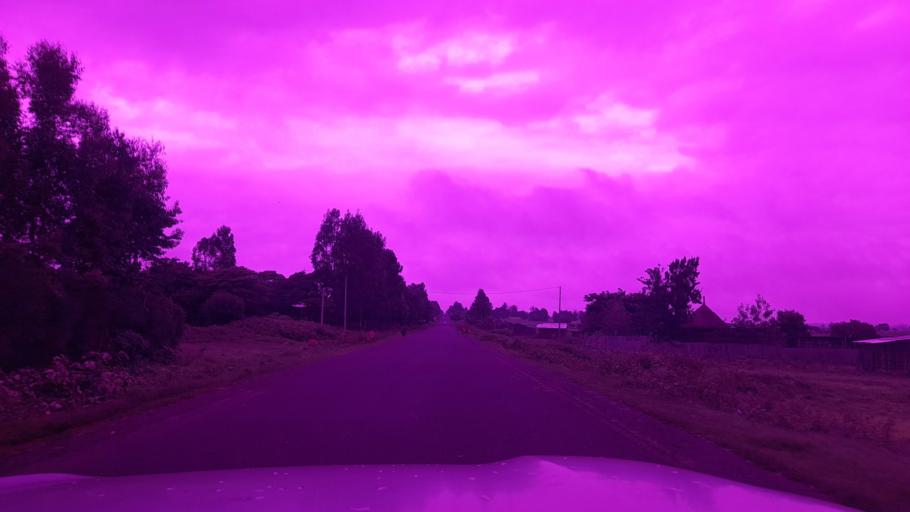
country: ET
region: Oromiya
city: Waliso
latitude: 8.2636
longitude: 37.6528
